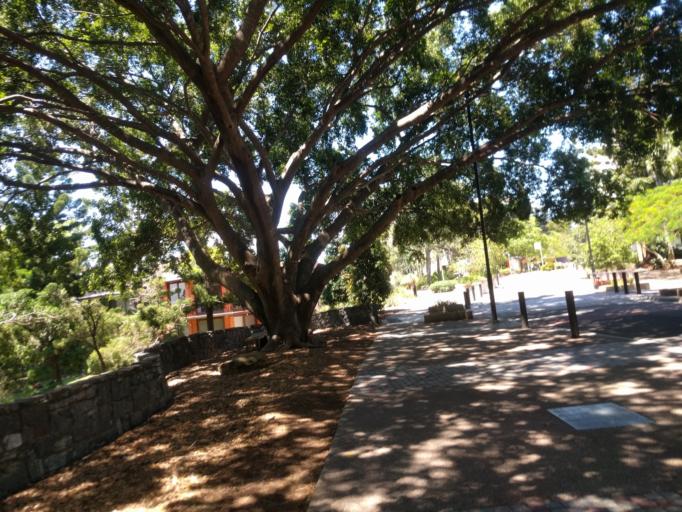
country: AU
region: Queensland
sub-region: Brisbane
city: Yeronga
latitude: -27.4980
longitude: 153.0148
